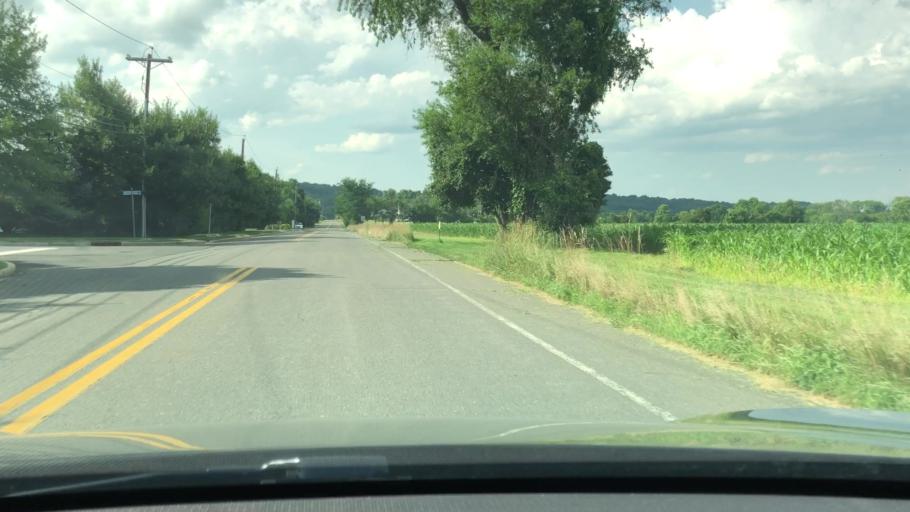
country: US
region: New Jersey
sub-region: Mercer County
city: Pennington
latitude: 40.3311
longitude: -74.8158
